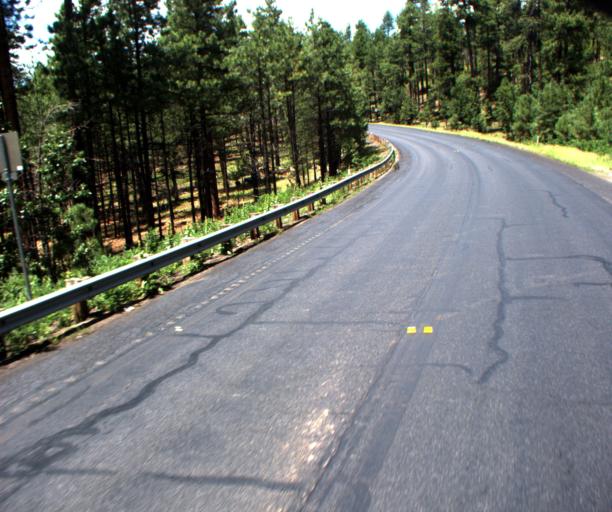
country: US
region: Arizona
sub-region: Gila County
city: Pine
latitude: 34.4635
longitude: -111.4429
